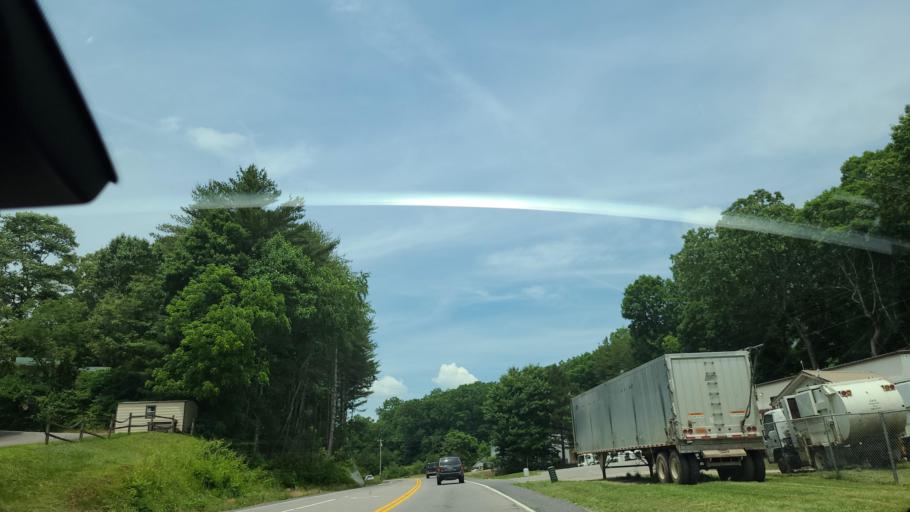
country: US
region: North Carolina
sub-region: Macon County
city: Franklin
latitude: 35.1769
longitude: -83.3455
